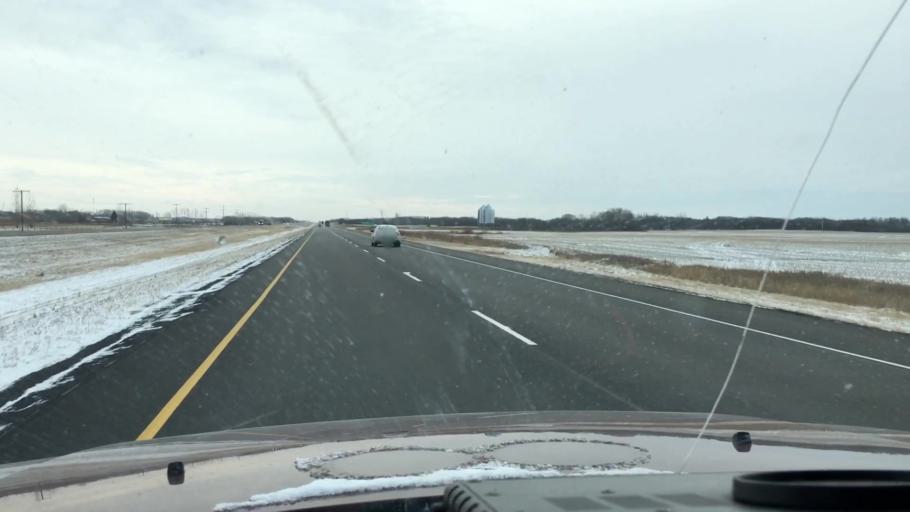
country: CA
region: Saskatchewan
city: Saskatoon
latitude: 52.0029
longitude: -106.5694
